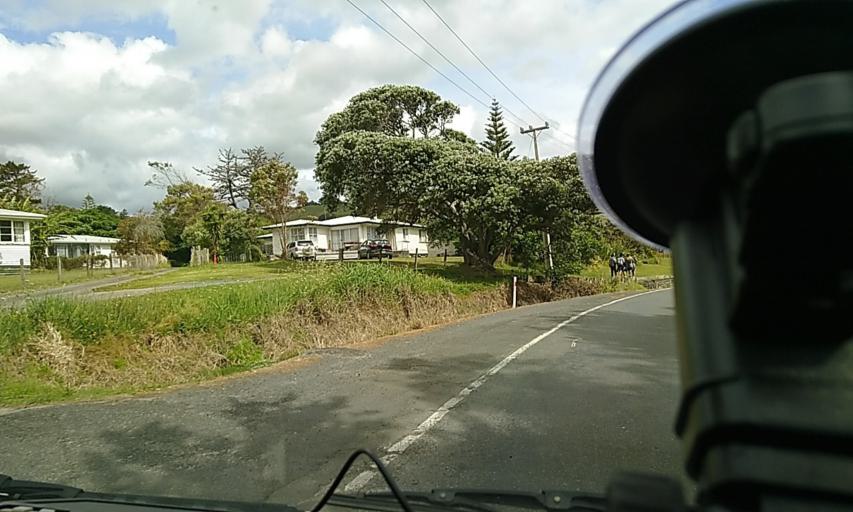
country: NZ
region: Northland
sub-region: Far North District
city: Ahipara
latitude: -35.5250
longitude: 173.3900
